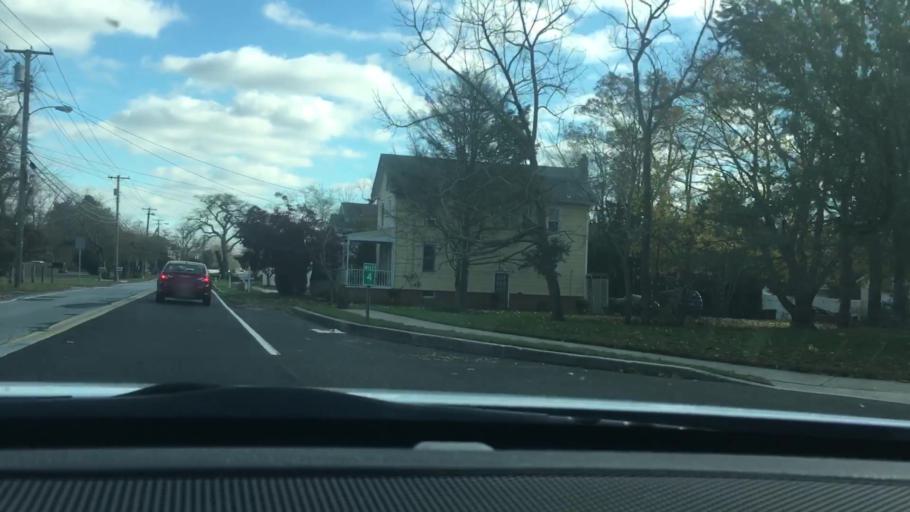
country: US
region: New Jersey
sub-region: Atlantic County
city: Northfield
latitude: 39.3747
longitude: -74.5699
